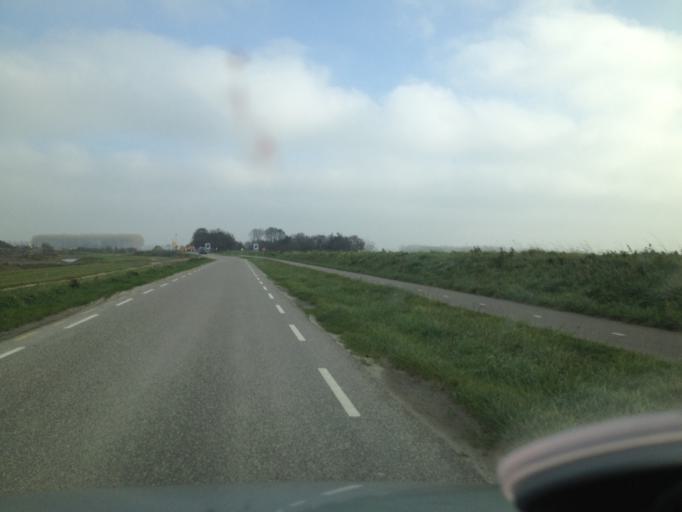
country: NL
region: Zeeland
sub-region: Gemeente Vlissingen
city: Vlissingen
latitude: 51.3954
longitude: 3.4995
